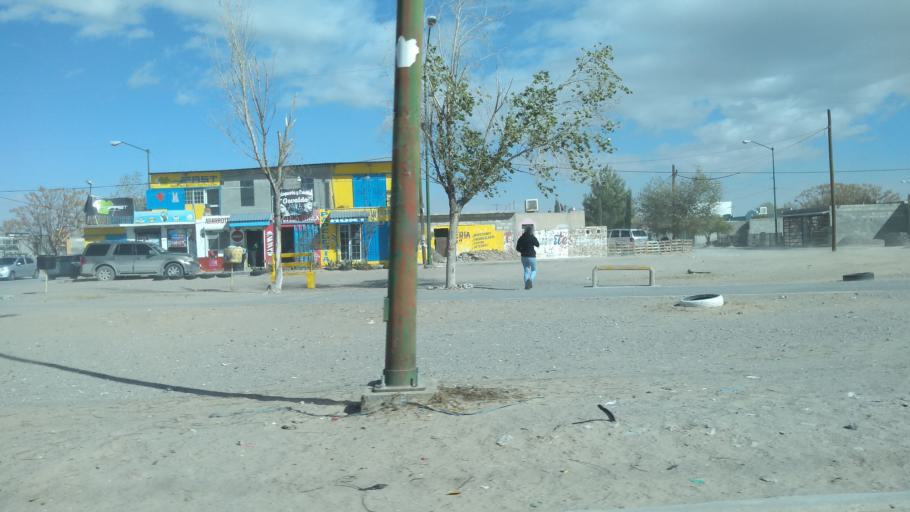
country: US
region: Texas
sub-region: El Paso County
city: Socorro Mission Number 1 Colonia
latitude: 31.5871
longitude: -106.3565
